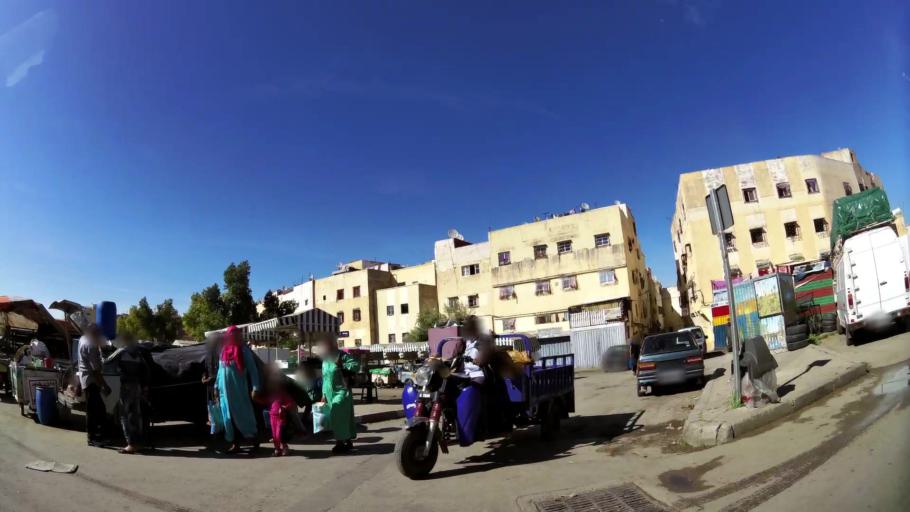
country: MA
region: Fes-Boulemane
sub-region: Fes
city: Fes
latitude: 34.0189
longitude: -4.9700
